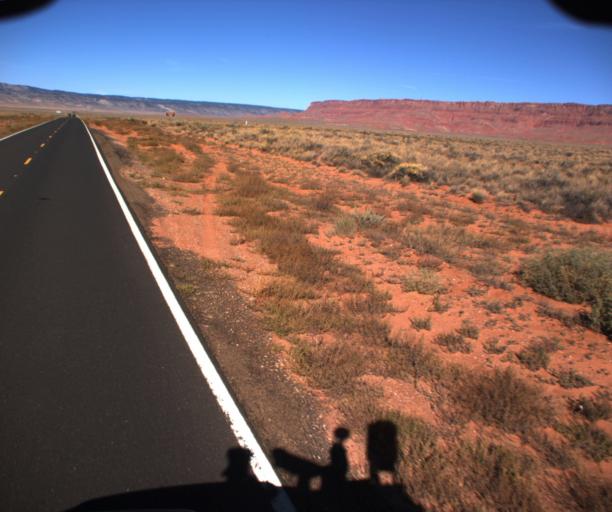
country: US
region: Arizona
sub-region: Coconino County
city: Page
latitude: 36.6954
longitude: -111.9062
